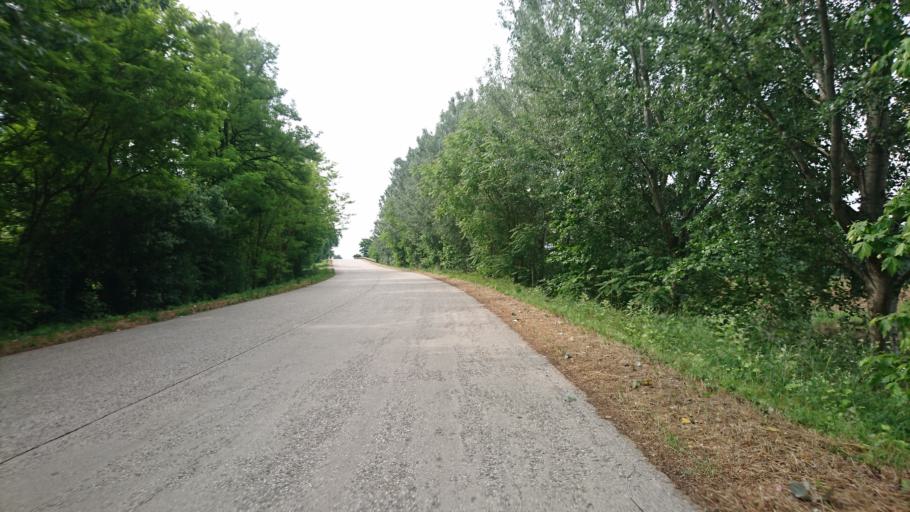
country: IT
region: Veneto
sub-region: Provincia di Padova
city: Monselice
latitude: 45.2297
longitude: 11.7200
